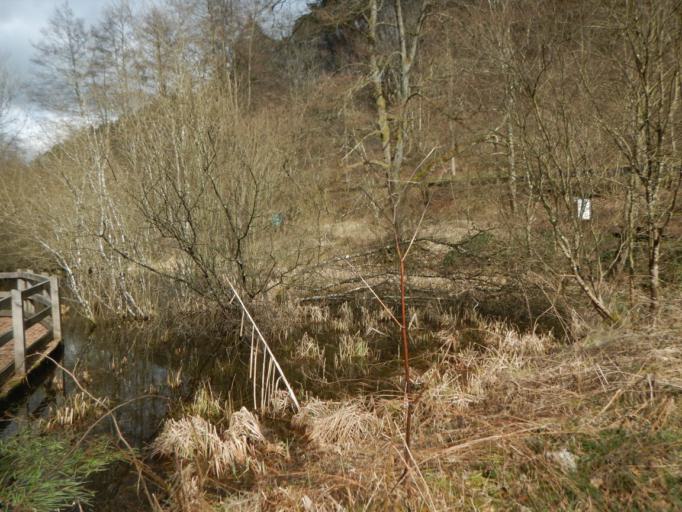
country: LU
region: Luxembourg
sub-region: Canton de Mersch
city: Tuntange
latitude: 49.7196
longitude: 6.0599
